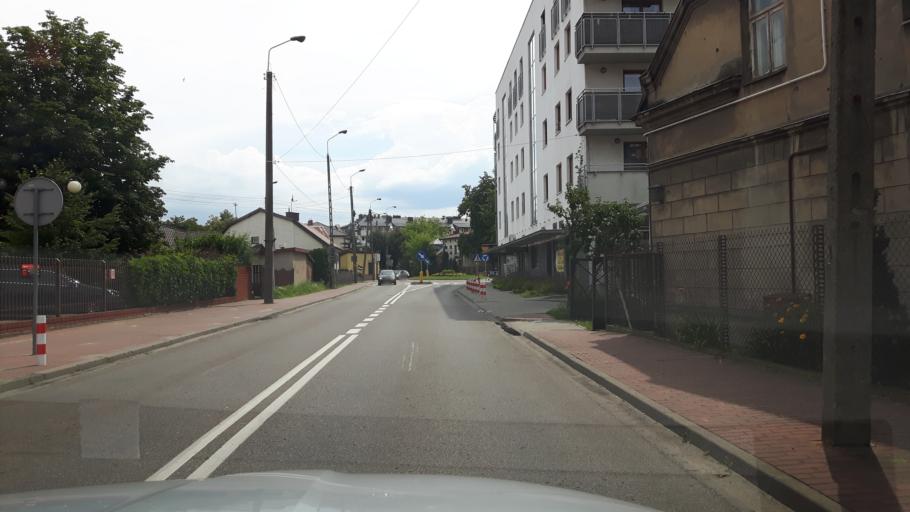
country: PL
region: Masovian Voivodeship
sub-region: Powiat wolominski
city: Wolomin
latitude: 52.3428
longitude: 21.2360
